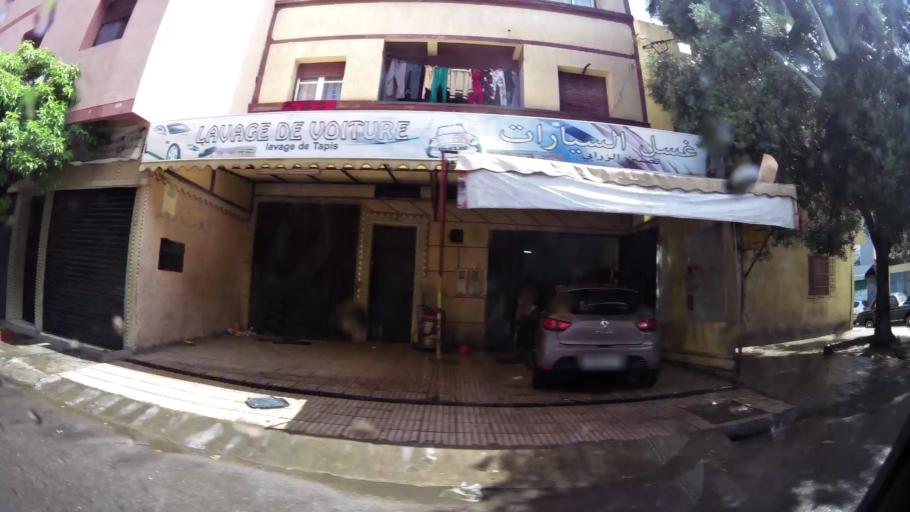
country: MA
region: Grand Casablanca
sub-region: Casablanca
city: Casablanca
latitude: 33.5511
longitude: -7.6776
